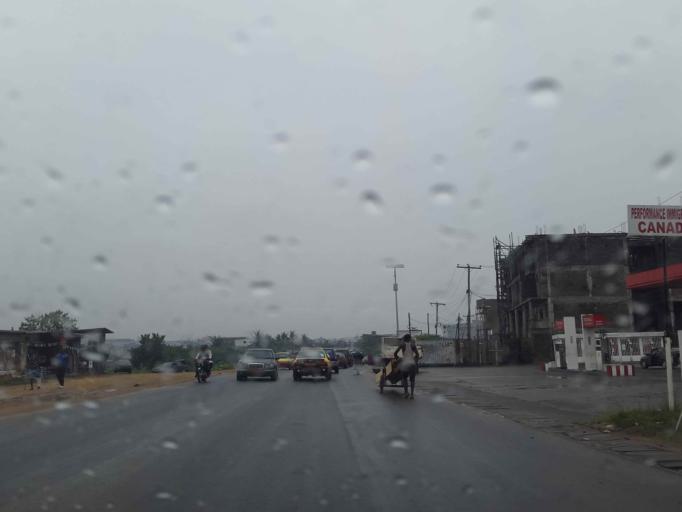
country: CM
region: Littoral
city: Douala
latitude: 4.0842
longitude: 9.7329
